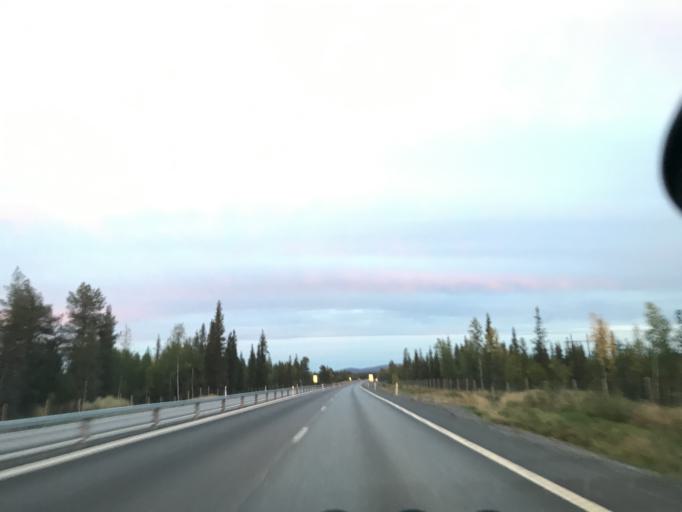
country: SE
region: Norrbotten
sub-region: Gallivare Kommun
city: Malmberget
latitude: 67.6915
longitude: 20.8289
